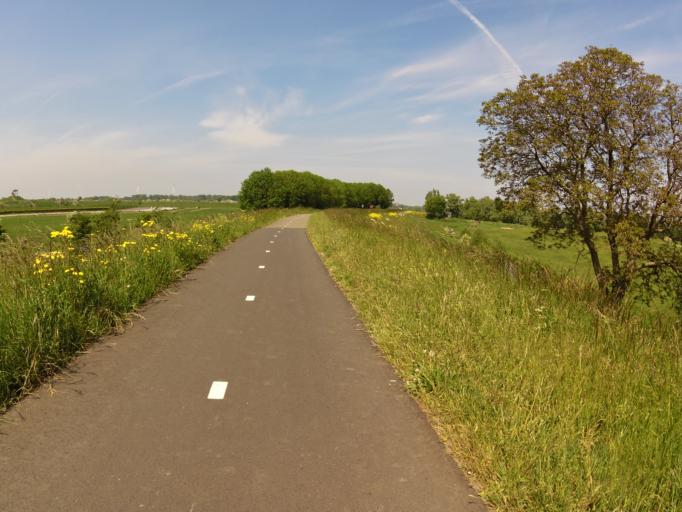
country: NL
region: Gelderland
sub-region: Gemeente Neerijnen
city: Neerijnen
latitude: 51.8138
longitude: 5.2824
